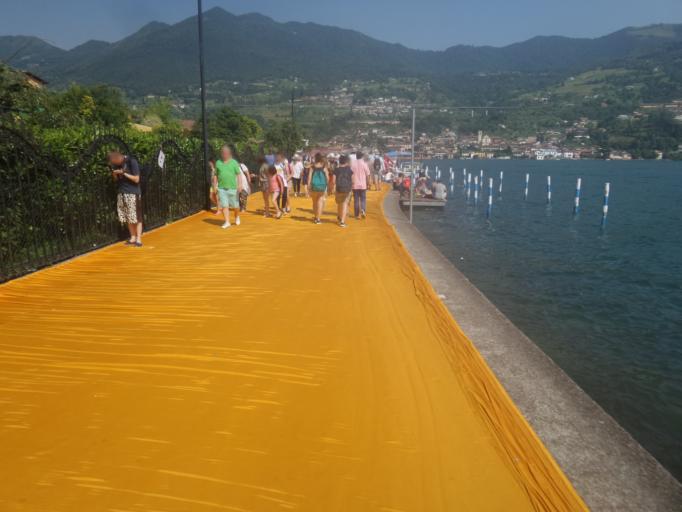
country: IT
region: Lombardy
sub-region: Provincia di Brescia
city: Sulzano
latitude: 45.6936
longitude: 10.0923
